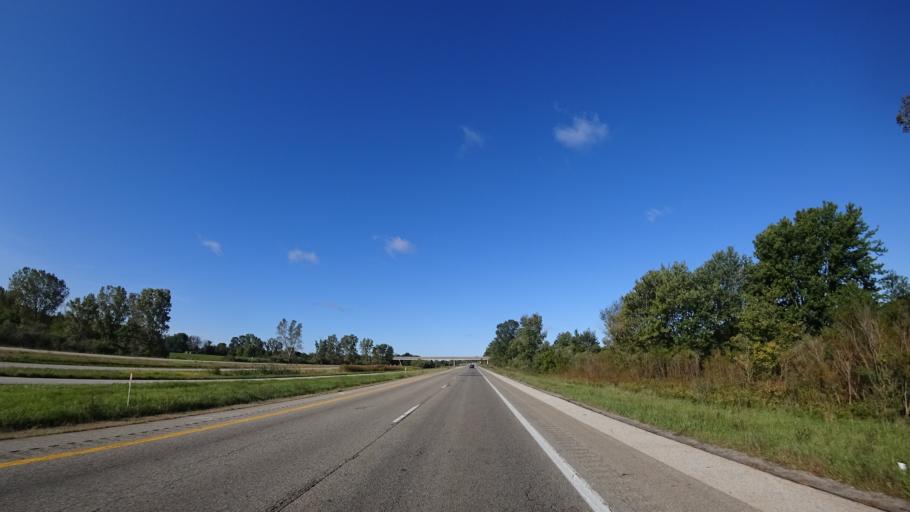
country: US
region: Michigan
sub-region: Ottawa County
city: Holland
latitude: 42.7349
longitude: -86.1322
